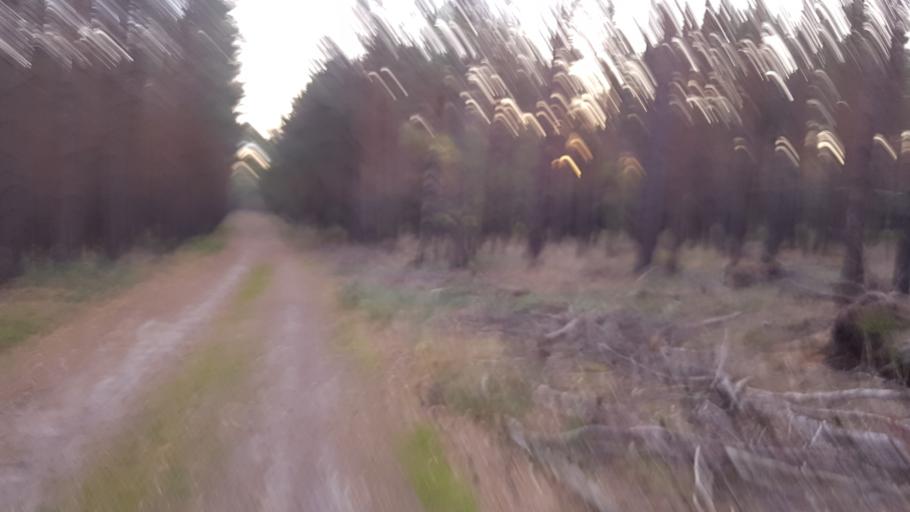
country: DE
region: Brandenburg
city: Trobitz
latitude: 51.5556
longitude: 13.4384
